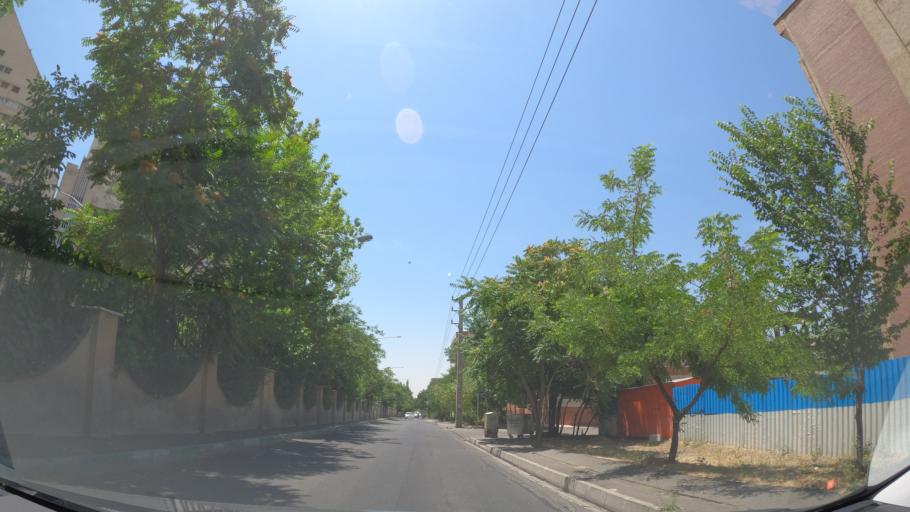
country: IR
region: Tehran
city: Tajrish
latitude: 35.7868
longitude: 51.3884
